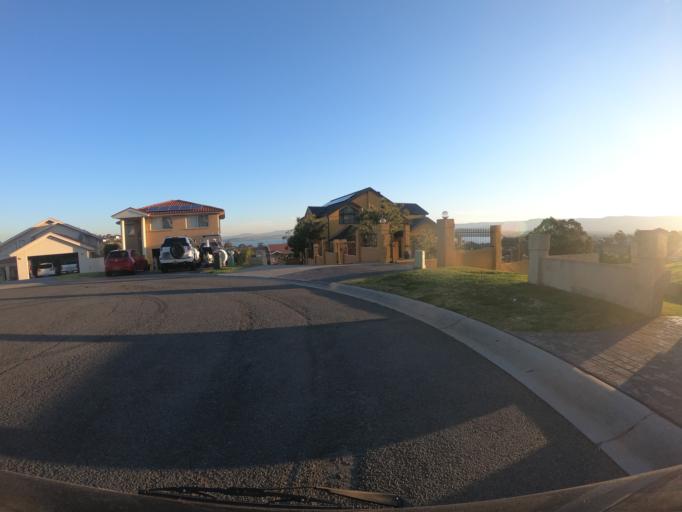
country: AU
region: New South Wales
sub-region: Wollongong
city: Berkeley
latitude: -34.4784
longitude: 150.8618
